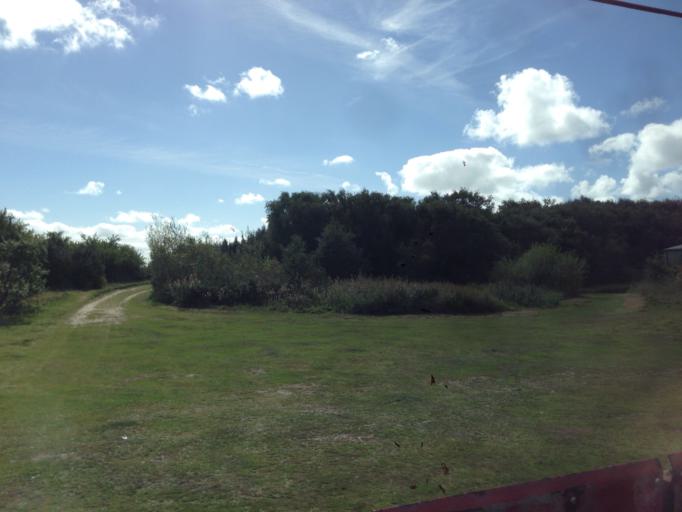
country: DE
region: Schleswig-Holstein
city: Sylt-Ost
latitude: 54.8702
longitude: 8.4676
